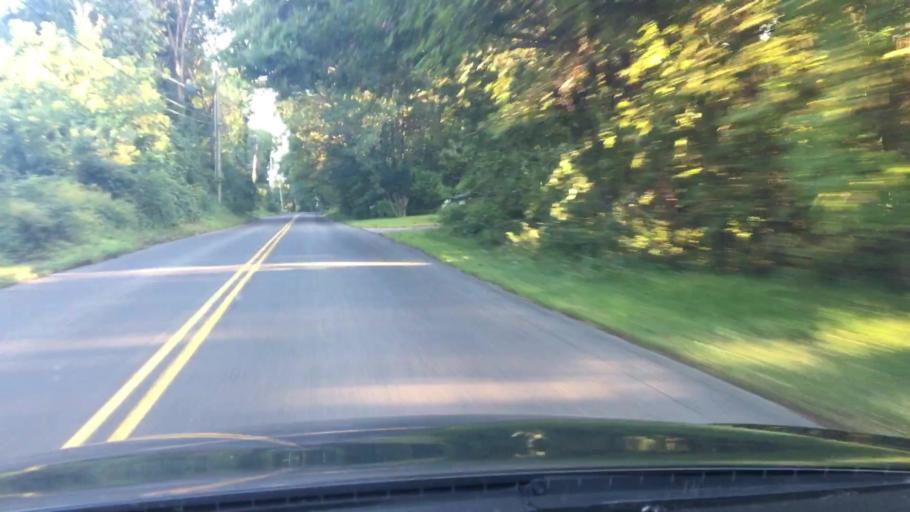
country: US
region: Connecticut
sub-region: Litchfield County
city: New Milford
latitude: 41.6167
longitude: -73.3733
